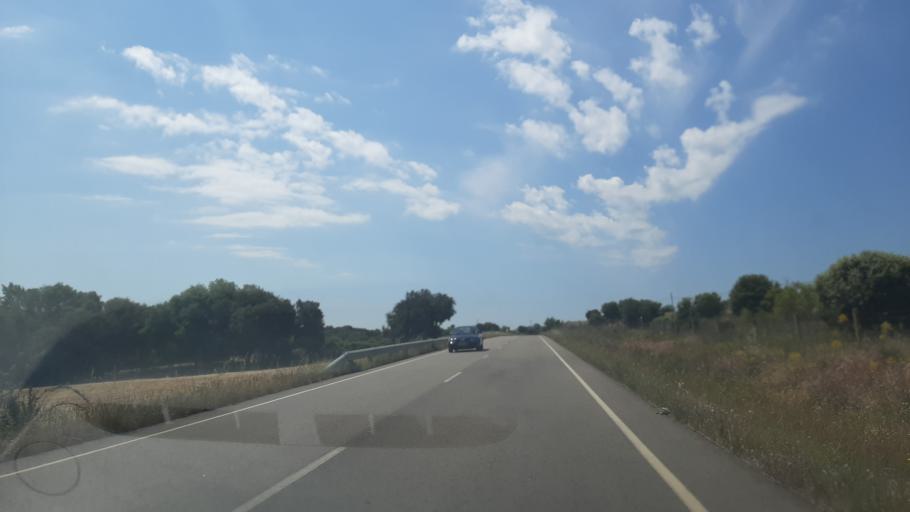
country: ES
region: Castille and Leon
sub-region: Provincia de Salamanca
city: Gallegos de Arganan
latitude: 40.6025
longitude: -6.7045
